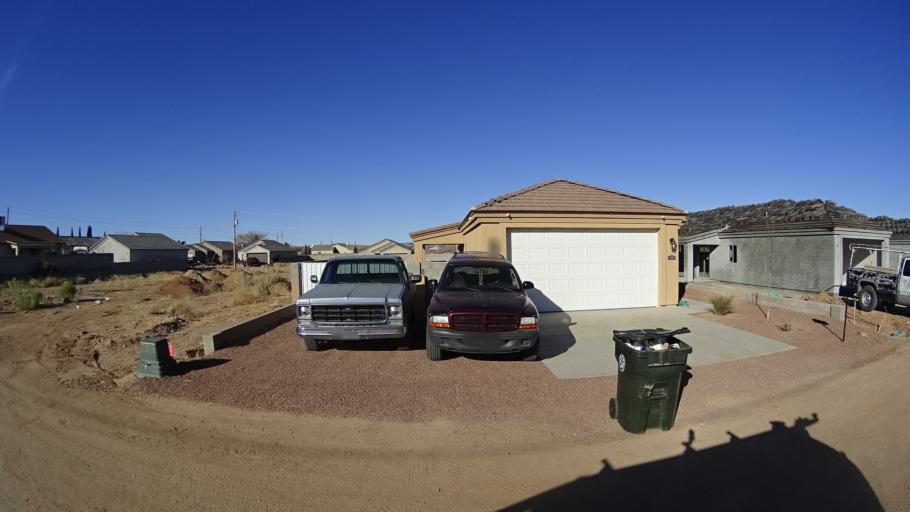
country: US
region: Arizona
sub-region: Mohave County
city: Kingman
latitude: 35.2110
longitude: -113.9943
